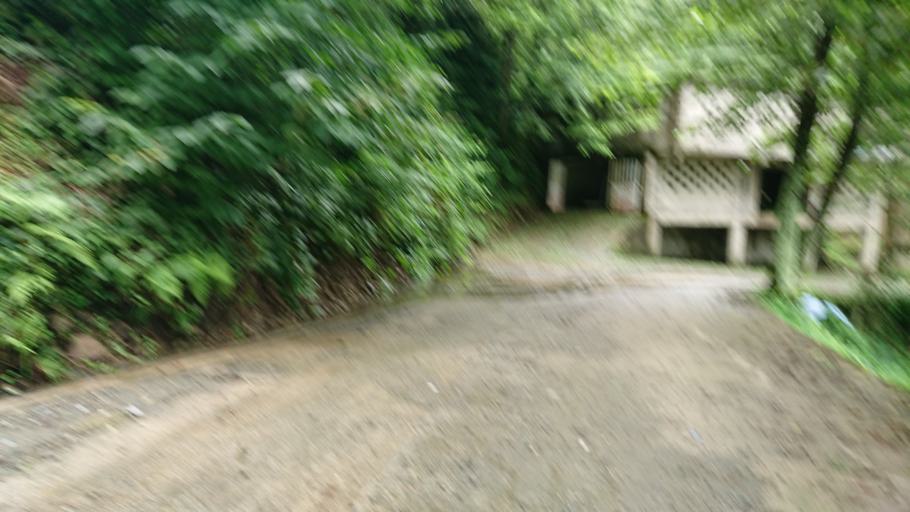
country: TR
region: Rize
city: Rize
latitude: 40.9770
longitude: 40.4851
